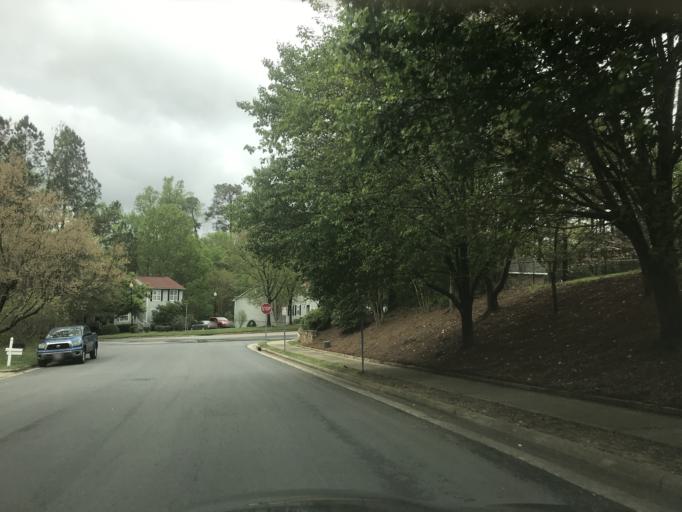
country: US
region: North Carolina
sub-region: Wake County
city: West Raleigh
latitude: 35.7497
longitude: -78.6851
